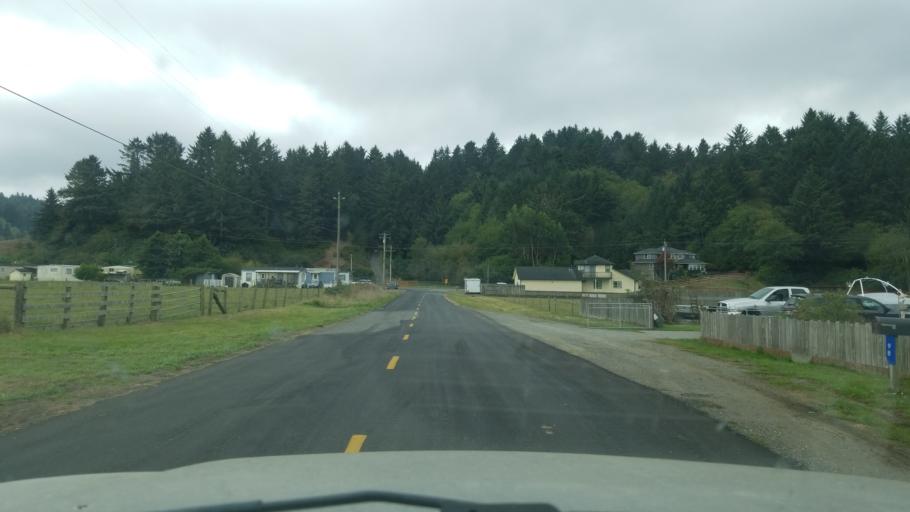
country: US
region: California
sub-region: Humboldt County
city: Ferndale
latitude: 40.5831
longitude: -124.2838
